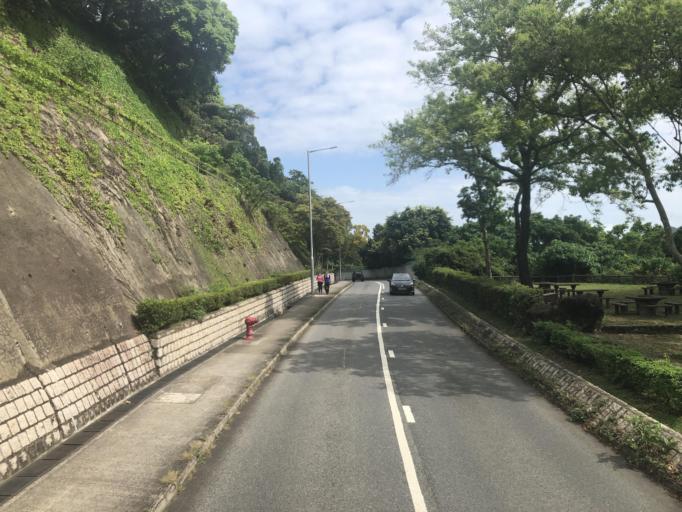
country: HK
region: Sai Kung
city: Sai Kung
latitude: 22.3905
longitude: 114.2908
